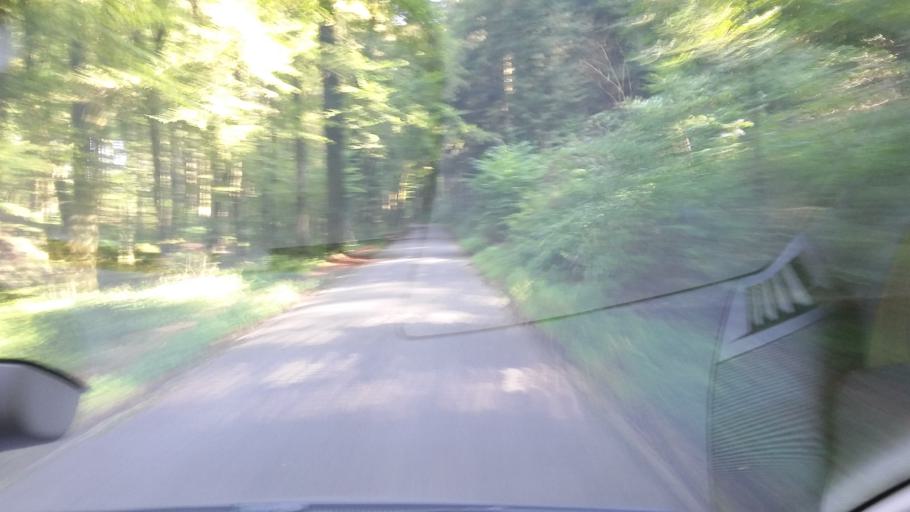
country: LU
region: Luxembourg
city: Eischen
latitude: 49.7049
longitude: 5.8593
